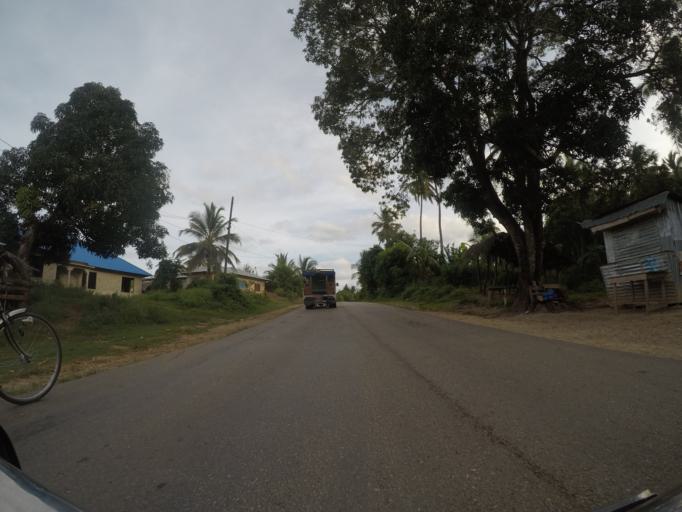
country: TZ
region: Pemba South
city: Chake Chake
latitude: -5.2738
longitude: 39.7705
